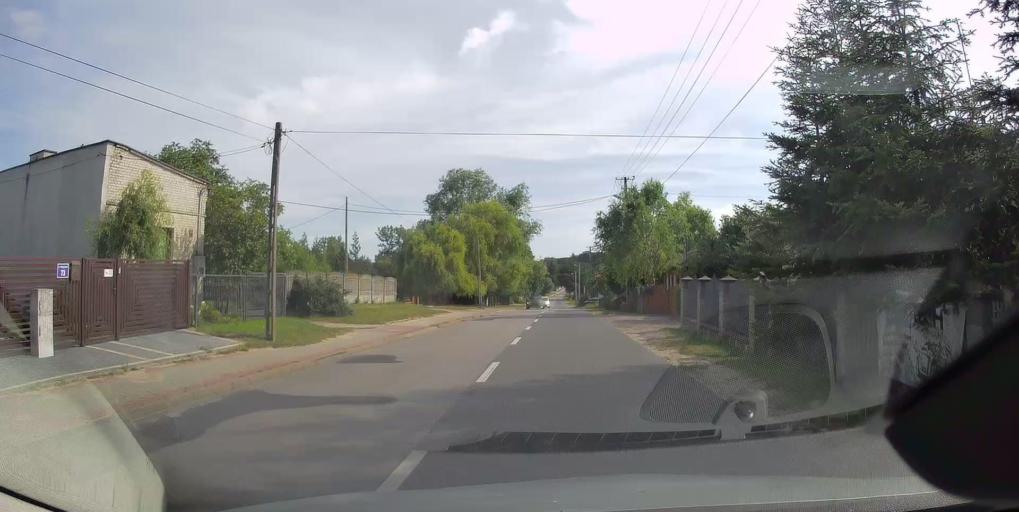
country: PL
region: Lodz Voivodeship
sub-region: Powiat tomaszowski
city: Tomaszow Mazowiecki
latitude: 51.4877
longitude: 19.9887
